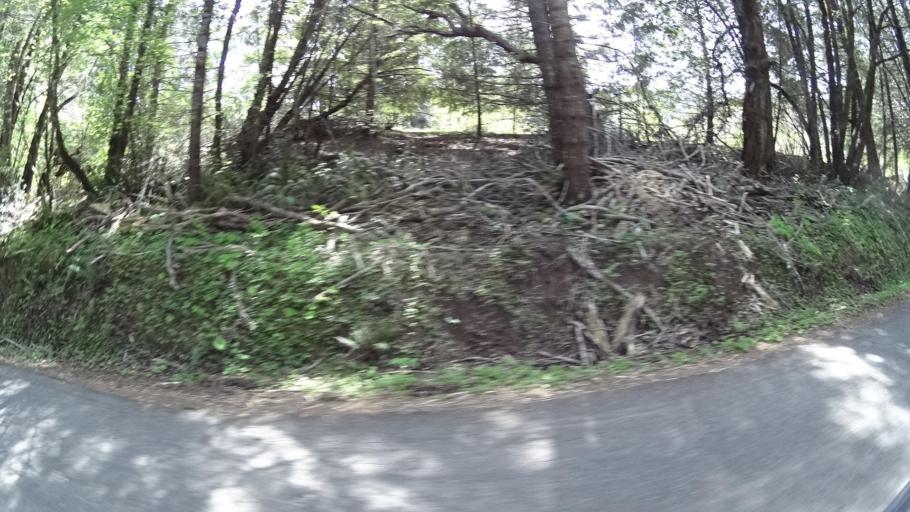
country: US
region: California
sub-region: Humboldt County
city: Redway
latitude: 40.3613
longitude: -123.7269
